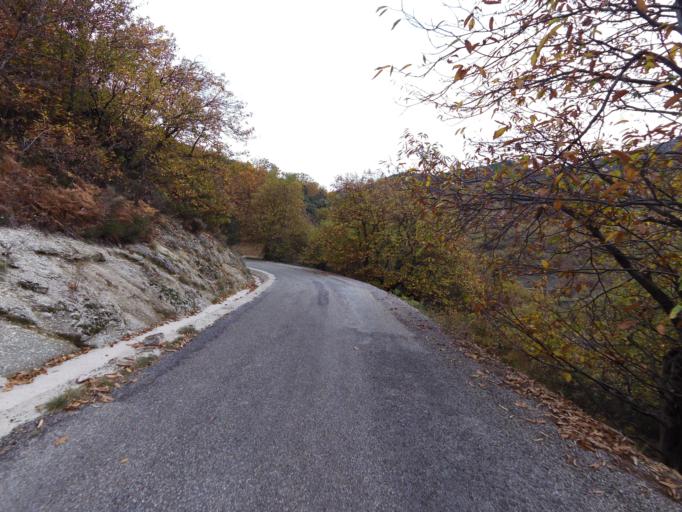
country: FR
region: Rhone-Alpes
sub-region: Departement de l'Ardeche
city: Les Vans
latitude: 44.4973
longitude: 4.0399
